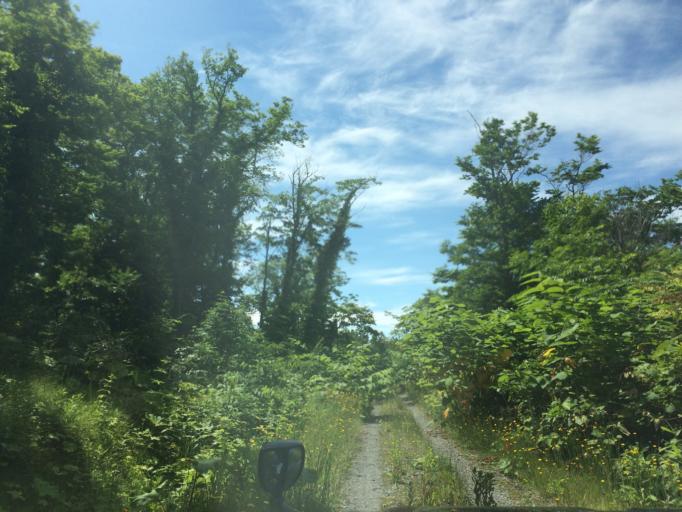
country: JP
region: Hokkaido
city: Niseko Town
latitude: 42.8644
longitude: 140.7914
